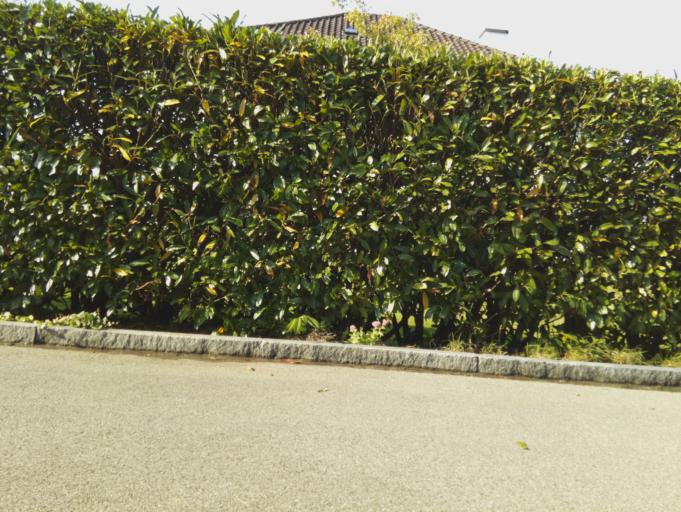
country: CH
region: Schwyz
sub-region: Bezirk March
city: Lachen
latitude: 47.1762
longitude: 8.8783
